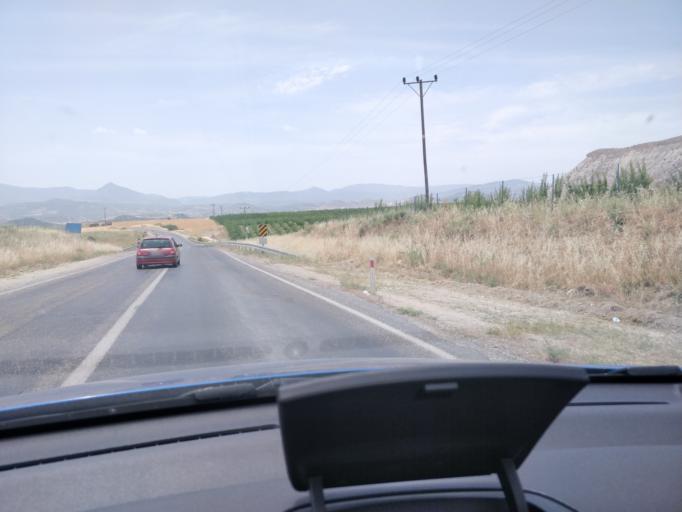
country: TR
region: Mersin
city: Mut
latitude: 36.5945
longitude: 33.4316
